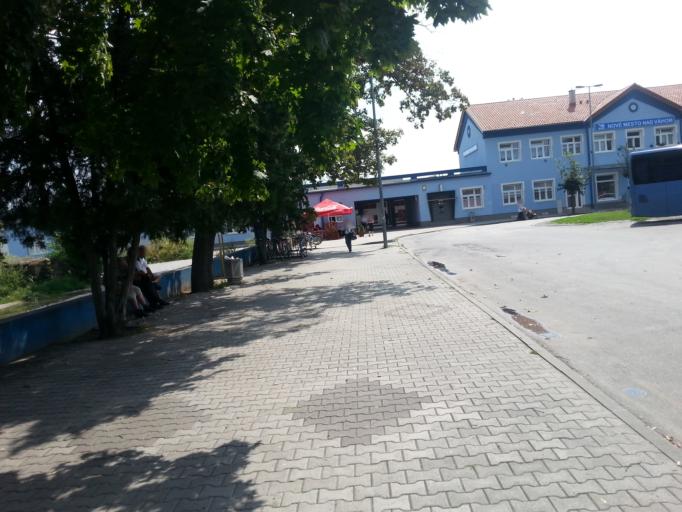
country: SK
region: Trenciansky
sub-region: Okres Nove Mesto nad Vahom
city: Nove Mesto nad Vahom
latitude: 48.7520
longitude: 17.8352
